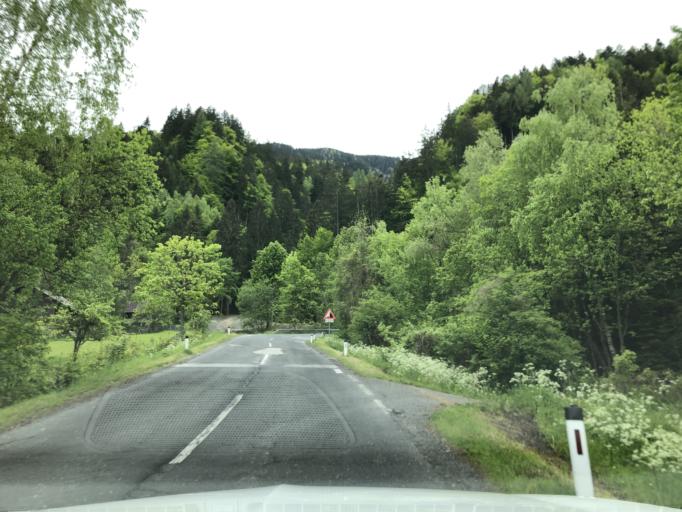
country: AT
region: Carinthia
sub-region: Politischer Bezirk Villach Land
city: Arnoldstein
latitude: 46.5400
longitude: 13.7721
